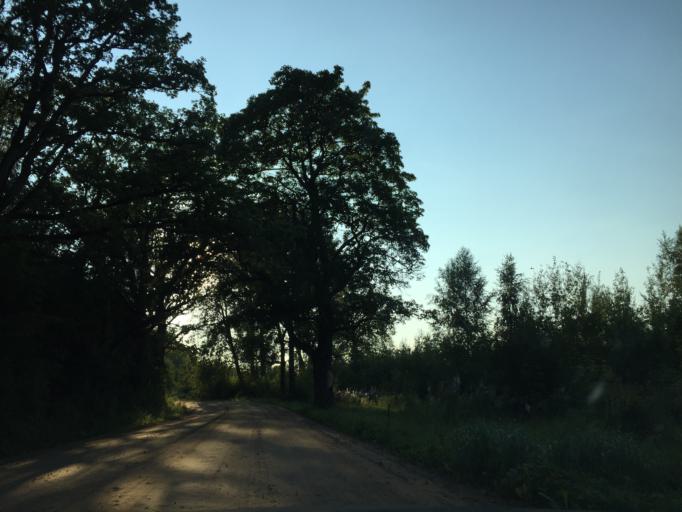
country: LV
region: Limbazu Rajons
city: Limbazi
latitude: 57.5506
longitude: 24.7923
